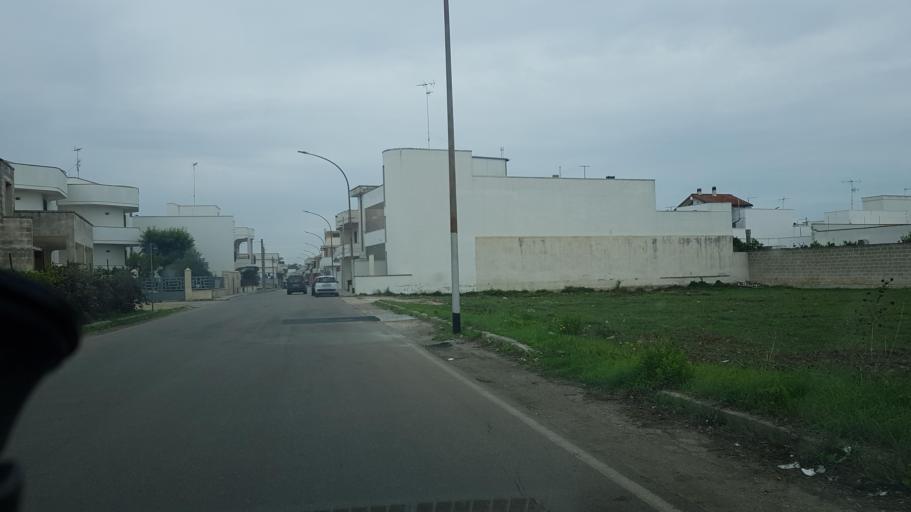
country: IT
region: Apulia
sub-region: Provincia di Lecce
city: Leverano
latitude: 40.2856
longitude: 17.9965
